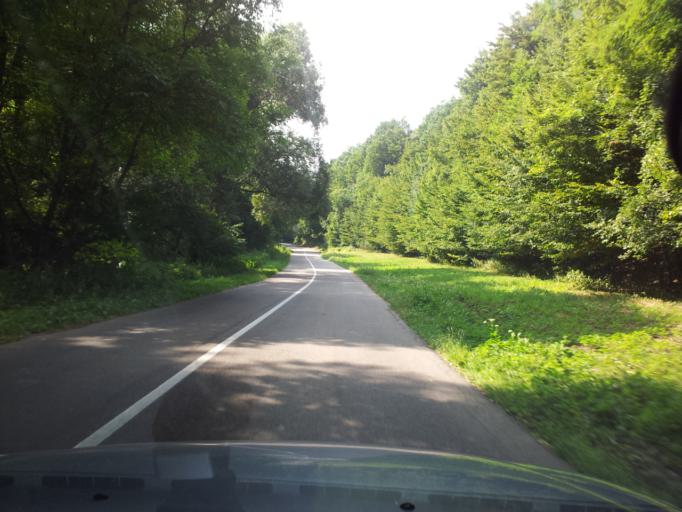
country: SK
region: Trenciansky
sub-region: Okres Trencin
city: Trencin
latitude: 48.8859
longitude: 18.0985
